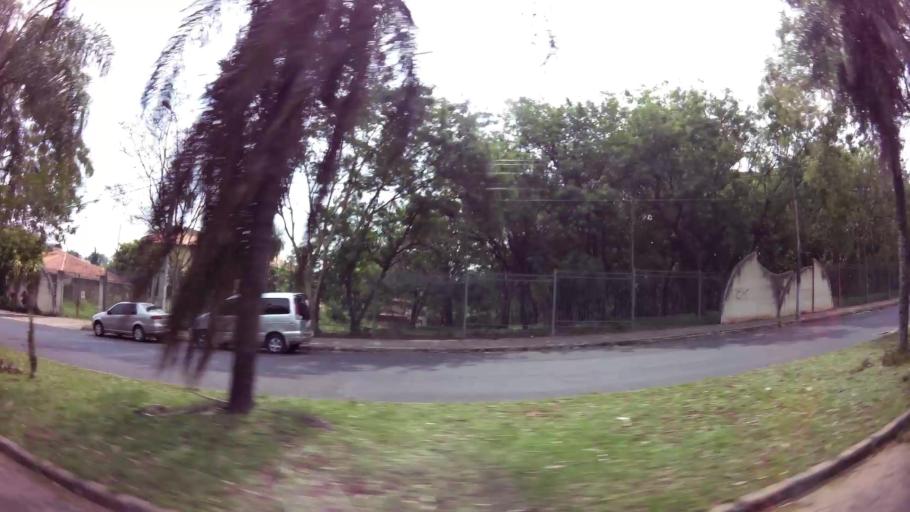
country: PY
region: Asuncion
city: Asuncion
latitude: -25.2793
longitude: -57.5791
